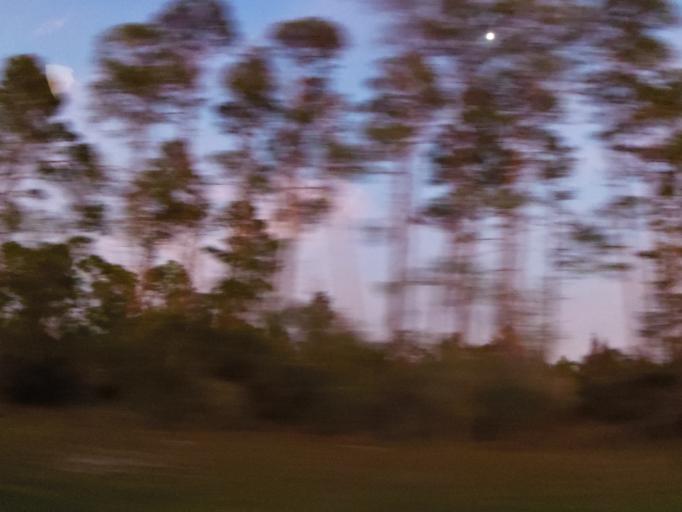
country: US
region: Florida
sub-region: Volusia County
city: De Leon Springs
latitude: 29.1829
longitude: -81.3047
